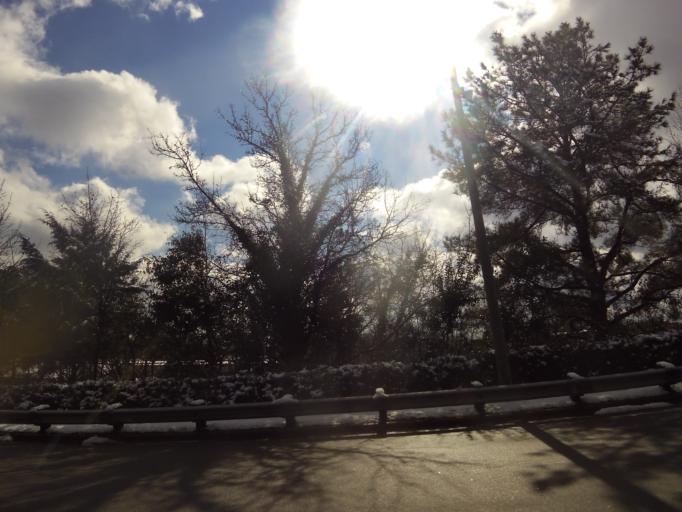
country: US
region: North Carolina
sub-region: Wilson County
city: Wilson
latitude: 35.7227
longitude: -77.9191
